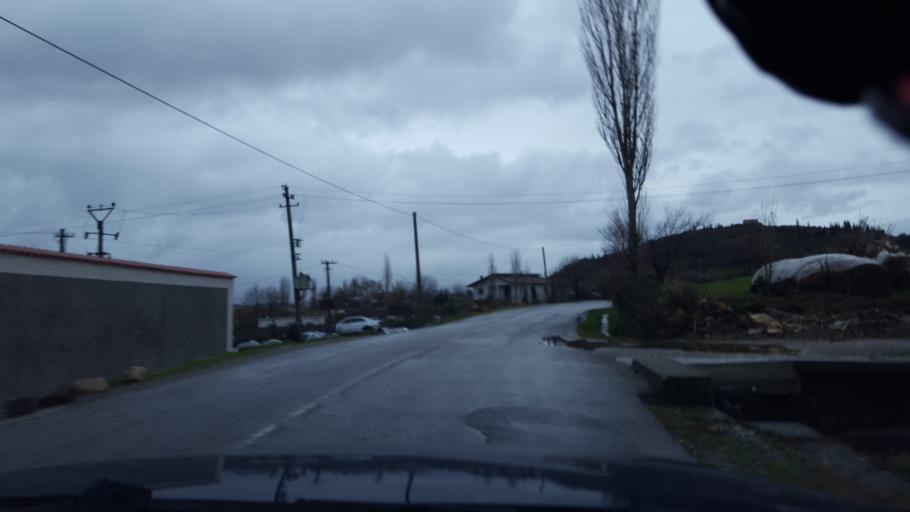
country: AL
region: Shkoder
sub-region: Rrethi i Shkodres
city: Berdica e Madhe
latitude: 42.0288
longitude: 19.4920
